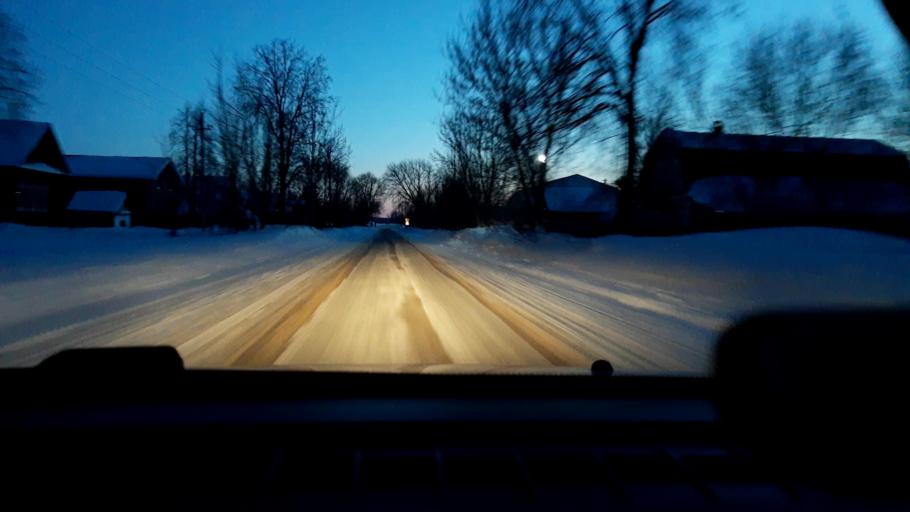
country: RU
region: Nizjnij Novgorod
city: Lyskovo
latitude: 56.1206
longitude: 45.3658
